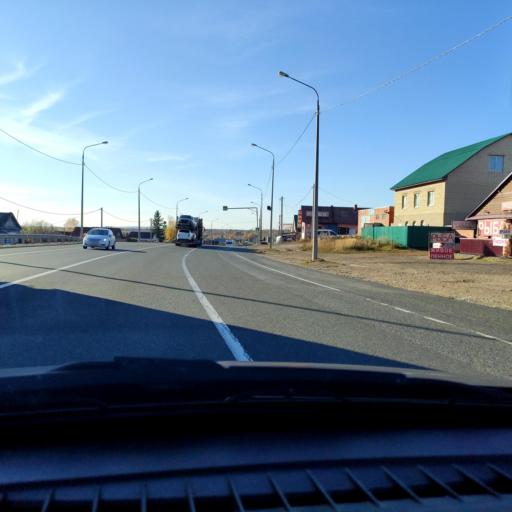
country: RU
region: Samara
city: Mezhdurechensk
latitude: 53.2480
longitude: 49.1833
